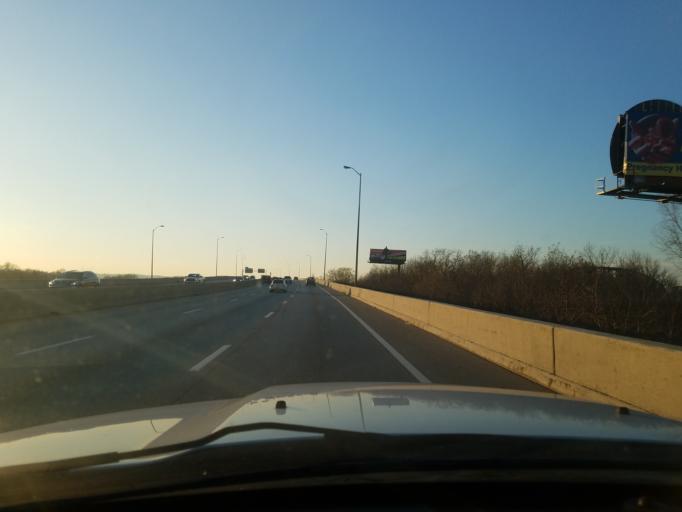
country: US
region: Indiana
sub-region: Floyd County
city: New Albany
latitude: 38.2770
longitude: -85.7963
